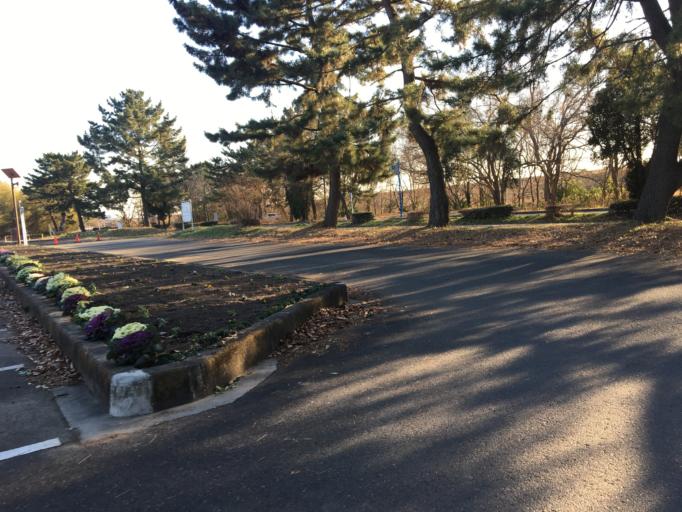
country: JP
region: Saitama
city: Shiki
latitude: 35.8494
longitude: 139.6015
